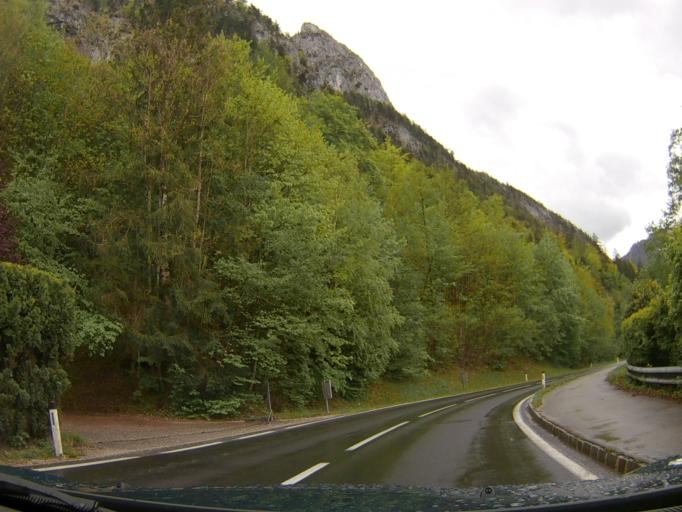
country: AT
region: Upper Austria
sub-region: Politischer Bezirk Vocklabruck
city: Steinbach am Attersee
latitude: 47.8056
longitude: 13.5480
